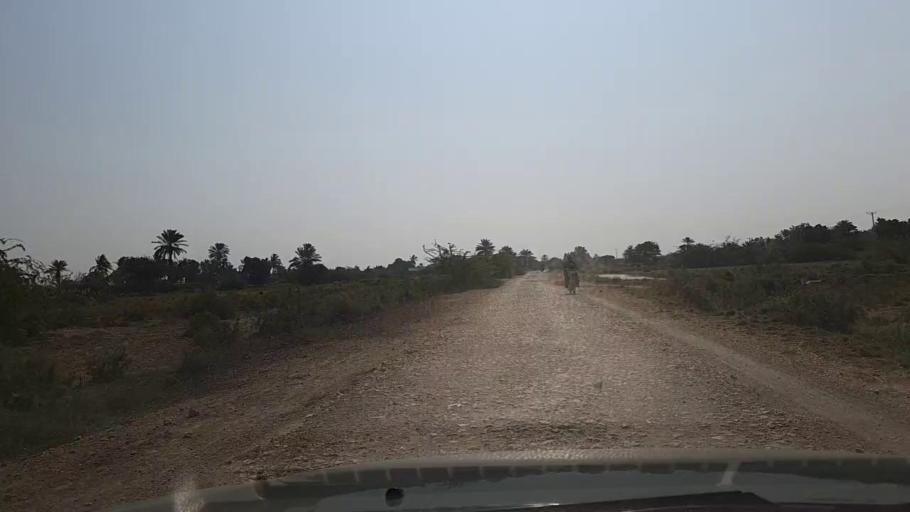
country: PK
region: Sindh
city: Mirpur Sakro
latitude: 24.3986
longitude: 67.6667
